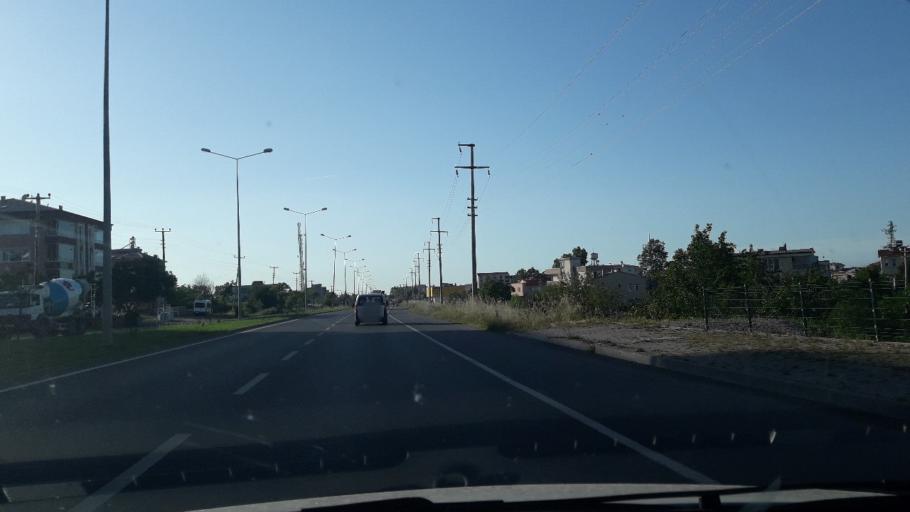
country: TR
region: Samsun
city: Taflan
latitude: 41.4091
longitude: 36.1778
